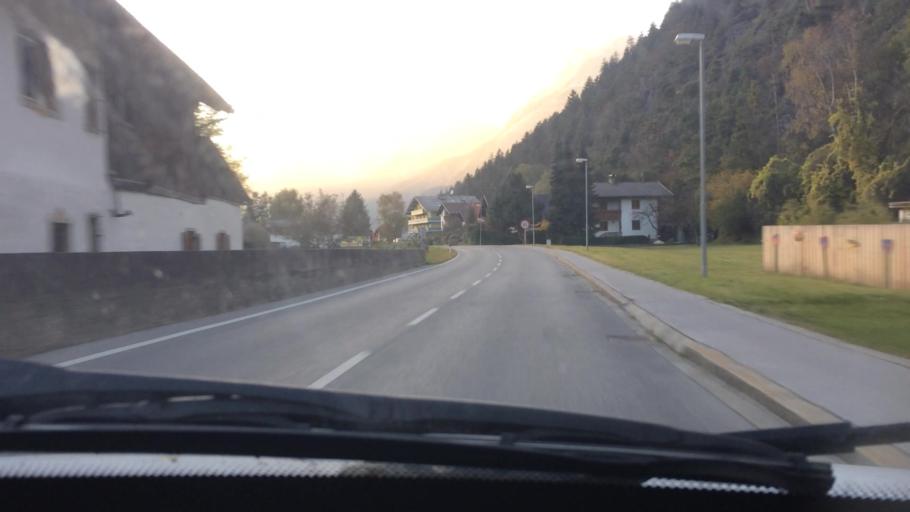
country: AT
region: Tyrol
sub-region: Politischer Bezirk Innsbruck Land
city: Hatting
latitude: 47.2922
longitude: 11.1595
